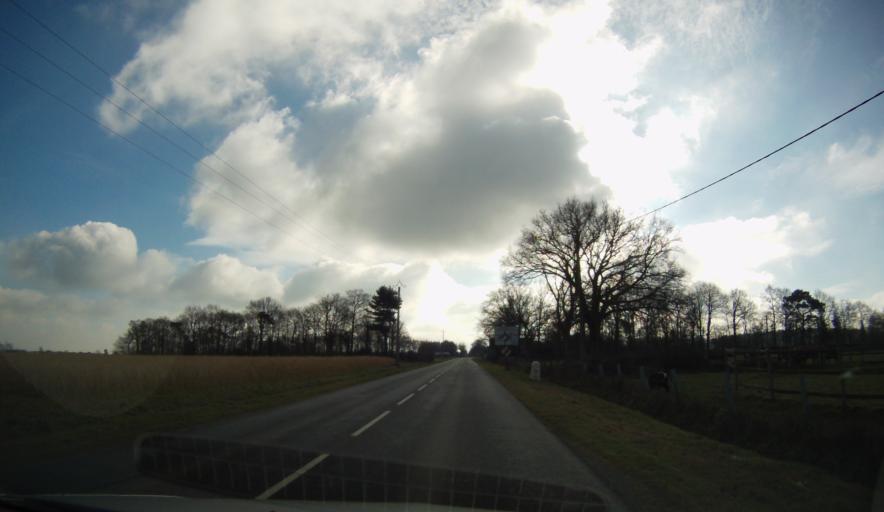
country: FR
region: Brittany
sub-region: Departement d'Ille-et-Vilaine
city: Tresboeuf
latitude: 47.9301
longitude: -1.5522
